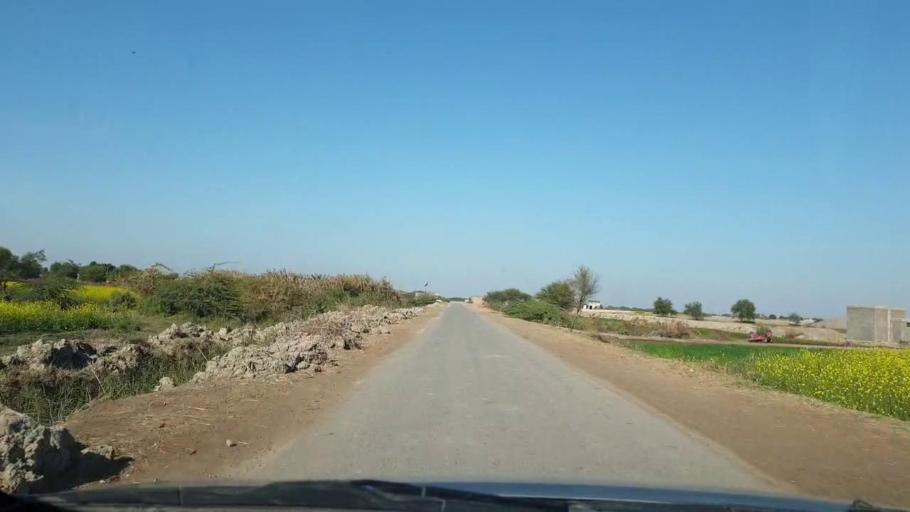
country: PK
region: Sindh
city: Jhol
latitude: 25.8311
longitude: 68.9505
